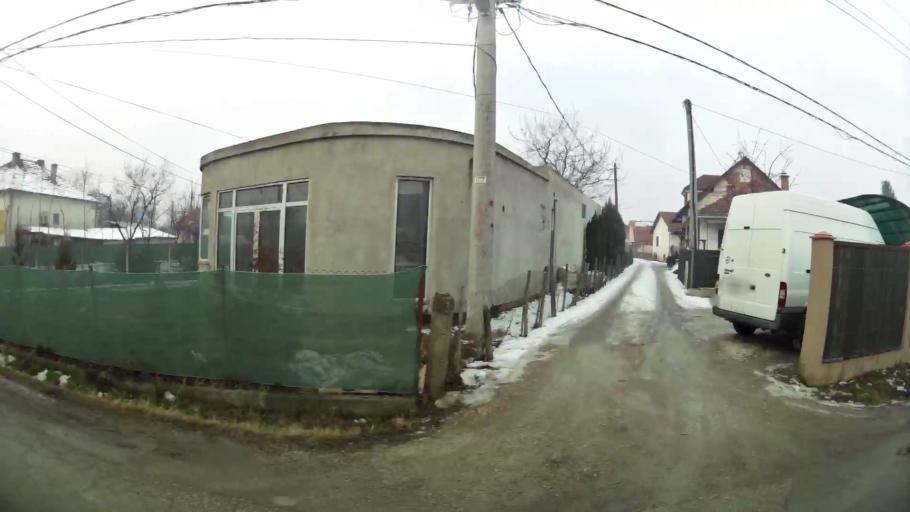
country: MK
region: Ilinden
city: Jurumleri
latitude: 41.9693
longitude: 21.5558
